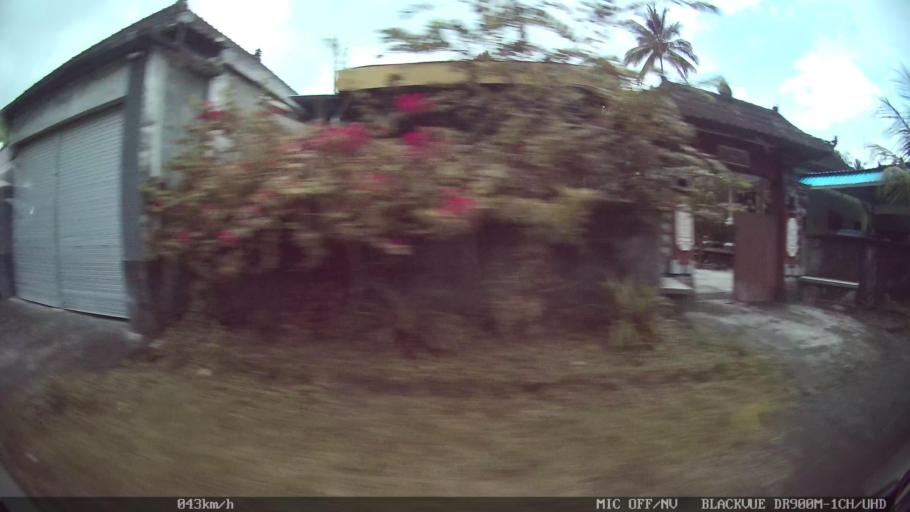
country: ID
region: Bali
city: Banjar Wangsian
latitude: -8.4458
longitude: 115.4242
